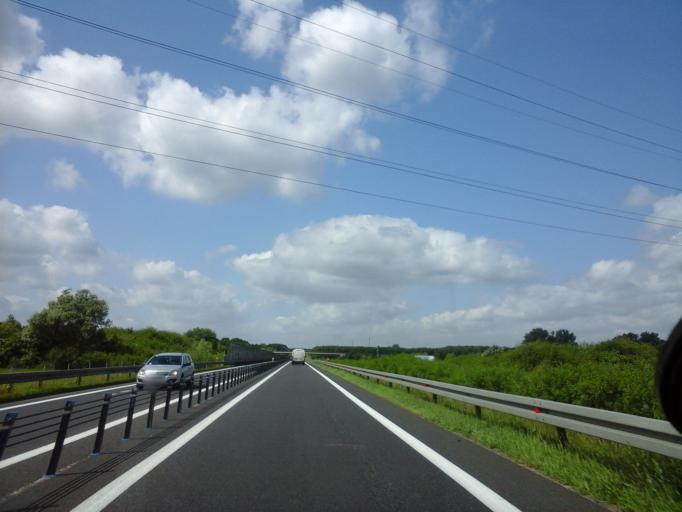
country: PL
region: West Pomeranian Voivodeship
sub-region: Powiat stargardzki
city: Kobylanka
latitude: 53.3575
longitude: 14.8754
